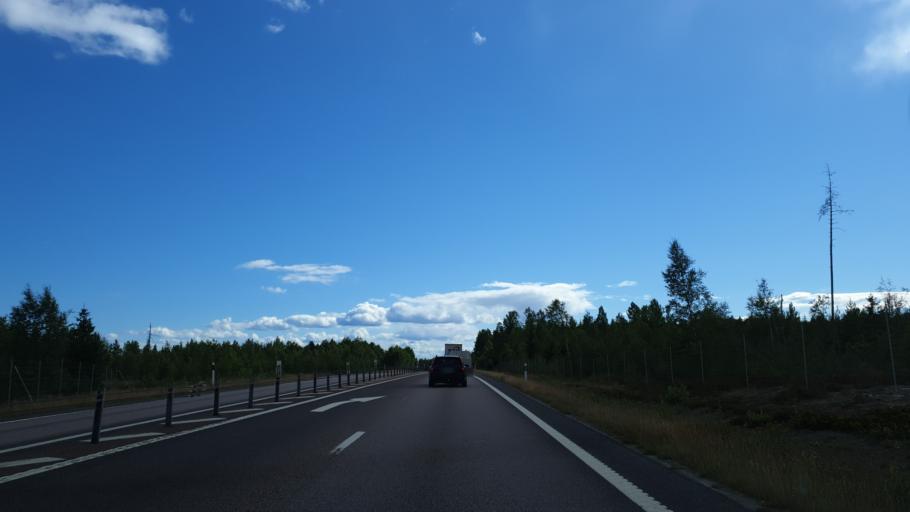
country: SE
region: Gaevleborg
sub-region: Hudiksvalls Kommun
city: Hudiksvall
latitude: 61.8507
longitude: 17.2020
